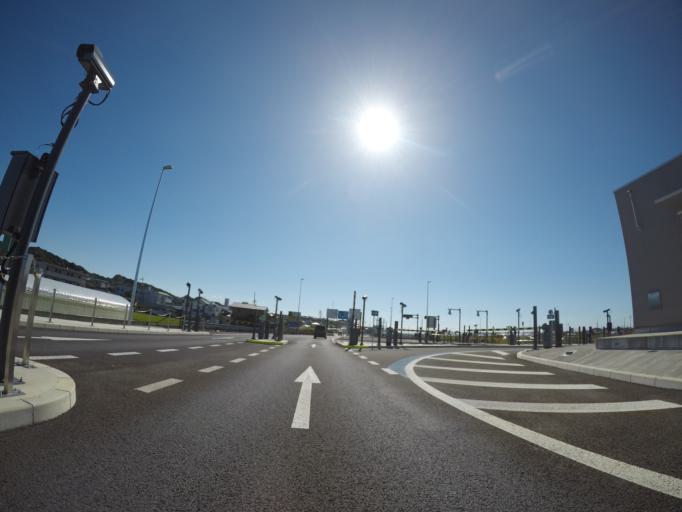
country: JP
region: Shizuoka
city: Shizuoka-shi
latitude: 34.9599
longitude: 138.4242
